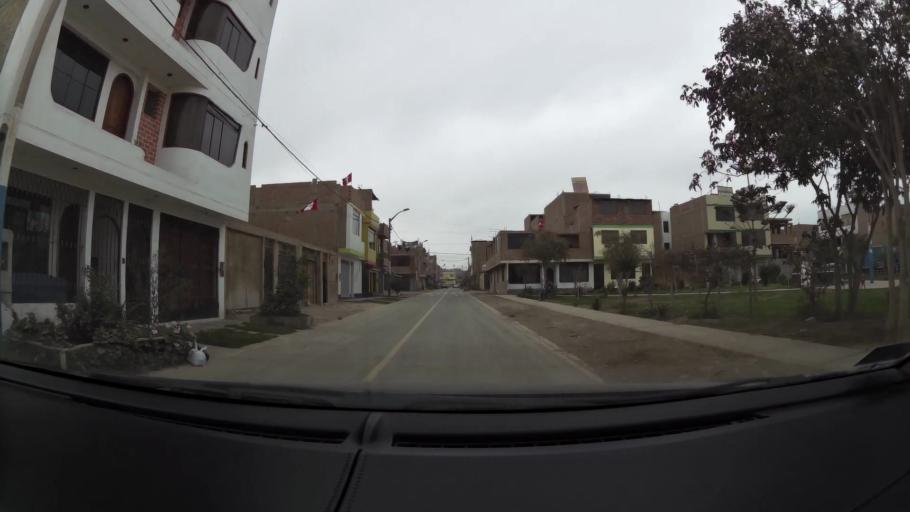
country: PE
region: Lima
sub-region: Lima
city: Independencia
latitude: -11.9712
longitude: -77.0930
